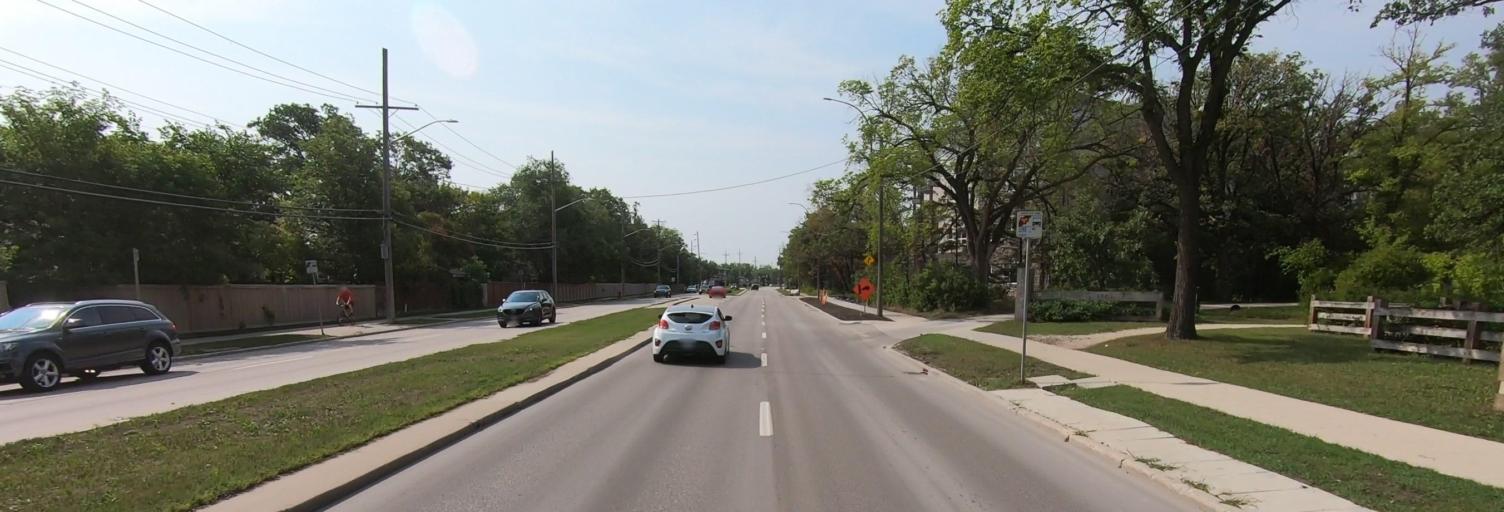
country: CA
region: Manitoba
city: Winnipeg
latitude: 49.8103
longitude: -97.1130
